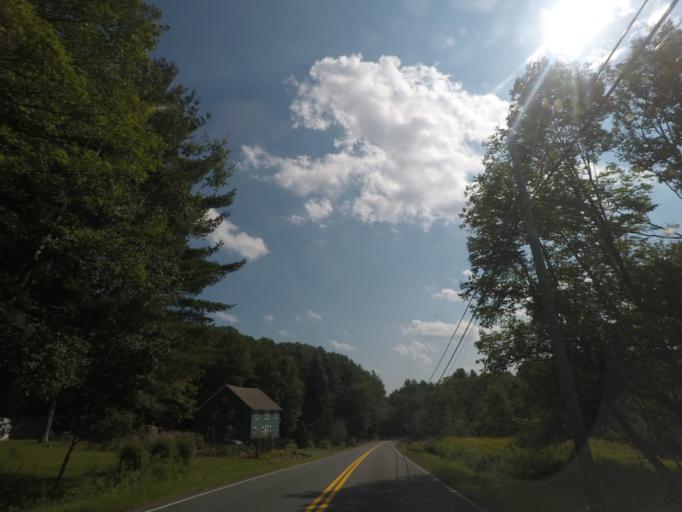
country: US
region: New York
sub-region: Rensselaer County
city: Poestenkill
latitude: 42.6953
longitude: -73.5169
